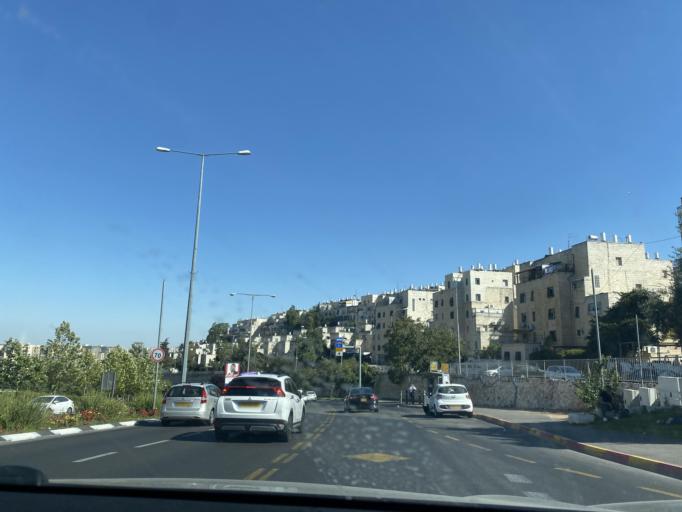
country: PS
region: West Bank
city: Bayt Iksa
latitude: 31.8215
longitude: 35.1894
